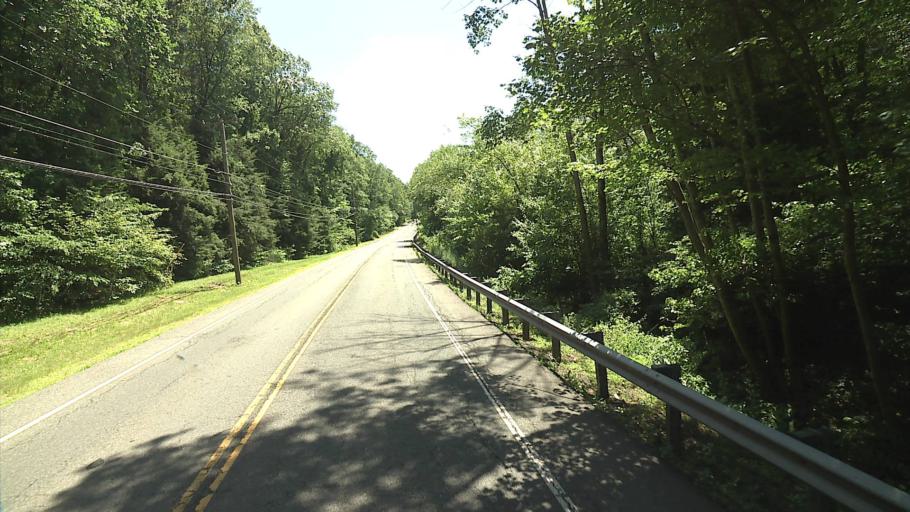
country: US
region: Massachusetts
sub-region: Hampden County
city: Southwick
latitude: 42.0093
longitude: -72.7255
